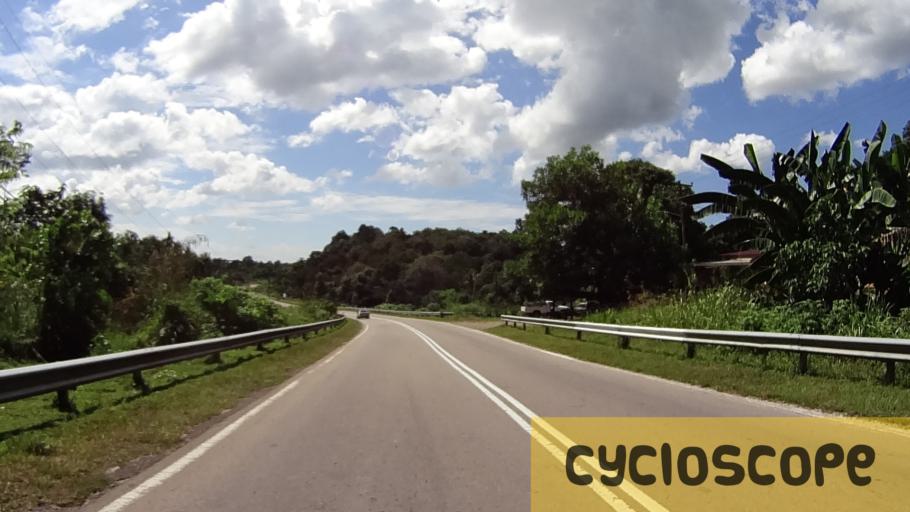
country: MY
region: Sabah
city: Beaufort
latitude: 5.1275
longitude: 115.6348
